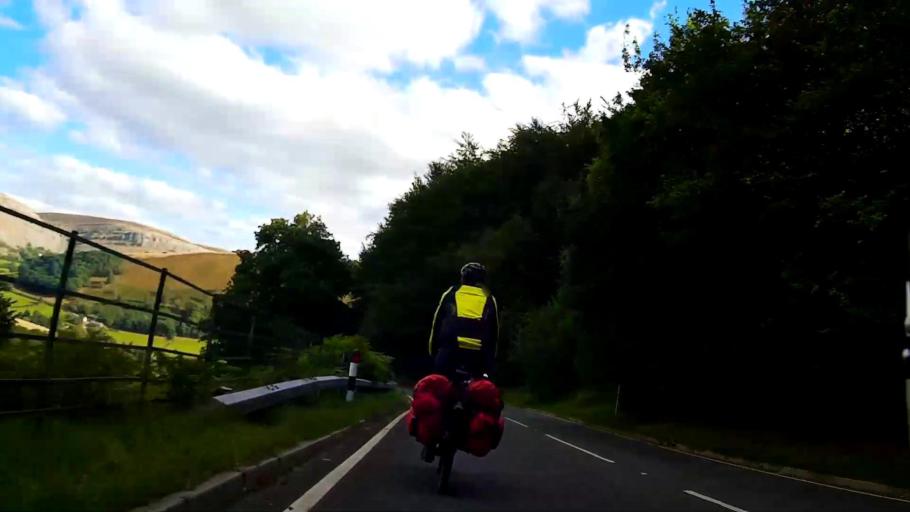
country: GB
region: Wales
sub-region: Denbighshire
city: Llangollen
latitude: 53.0076
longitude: -3.1950
